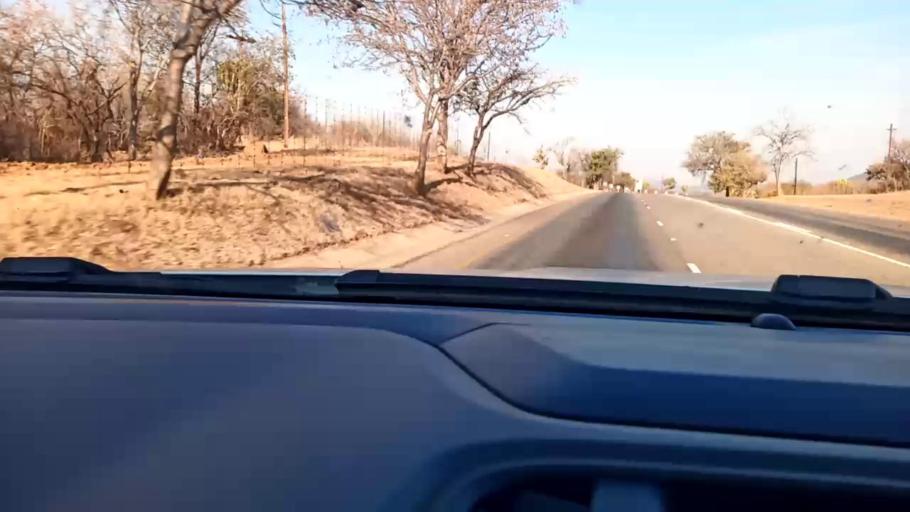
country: ZA
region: Limpopo
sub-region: Mopani District Municipality
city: Duiwelskloof
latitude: -23.6199
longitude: 30.1243
